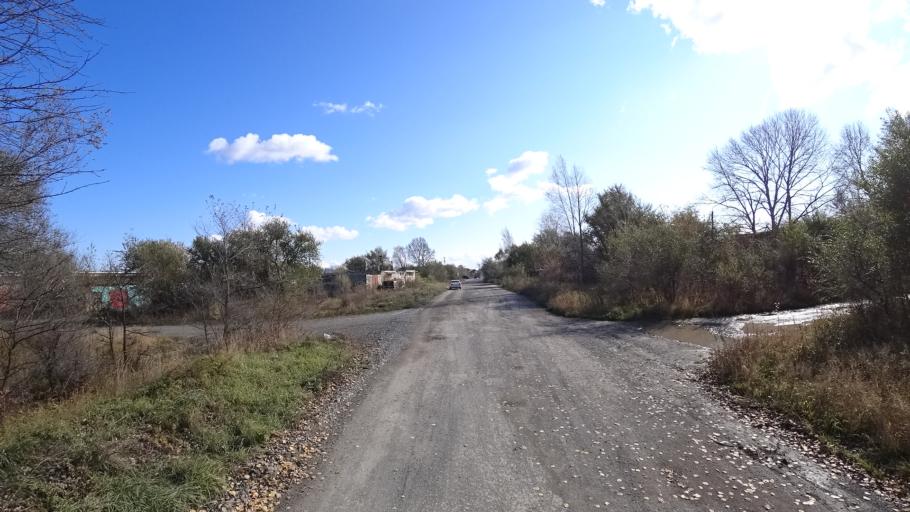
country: RU
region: Khabarovsk Krai
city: Amursk
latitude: 50.1023
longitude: 136.5051
